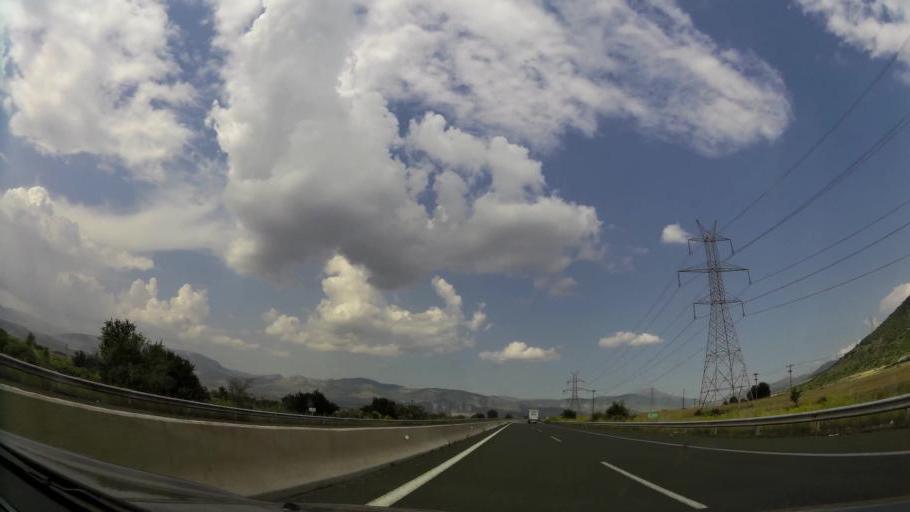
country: GR
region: West Macedonia
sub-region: Nomos Kozanis
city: Kleitos
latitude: 40.3687
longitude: 21.8733
